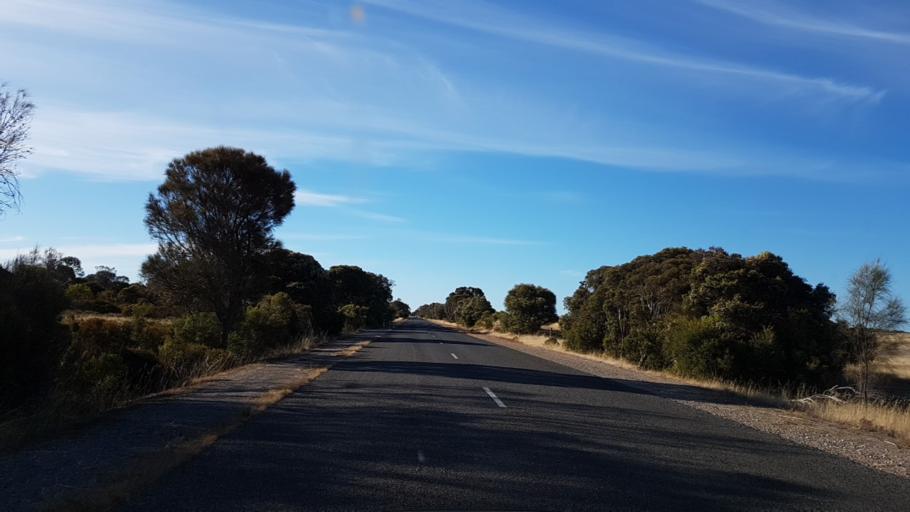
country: AU
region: South Australia
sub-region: Yorke Peninsula
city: Honiton
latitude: -34.9372
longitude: 137.0908
